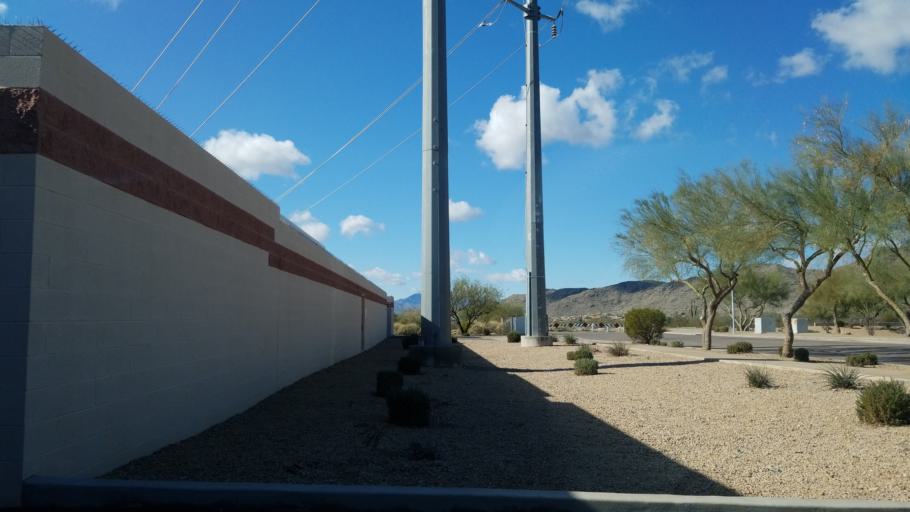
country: US
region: Arizona
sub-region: Maricopa County
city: Laveen
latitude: 33.2944
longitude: -112.0996
